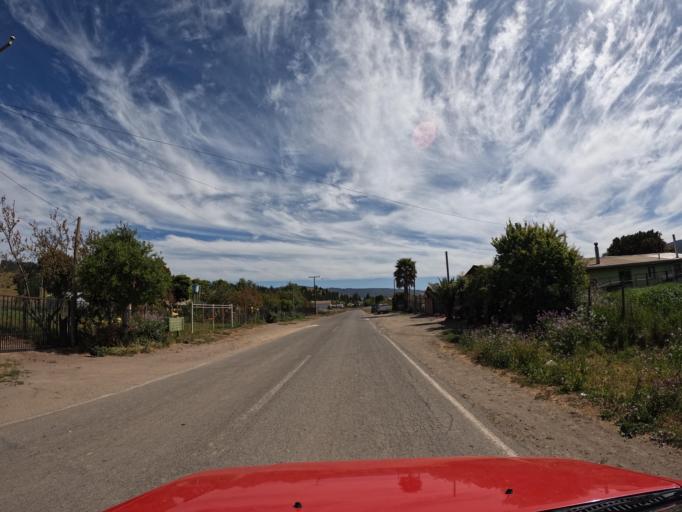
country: CL
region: Maule
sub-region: Provincia de Talca
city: Constitucion
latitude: -35.0263
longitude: -72.0463
